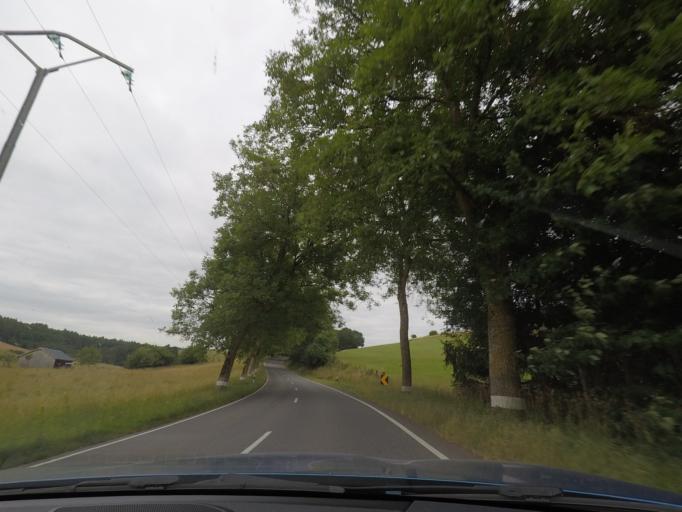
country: LU
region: Diekirch
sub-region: Canton de Vianden
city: Vianden
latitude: 49.9149
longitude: 6.2106
